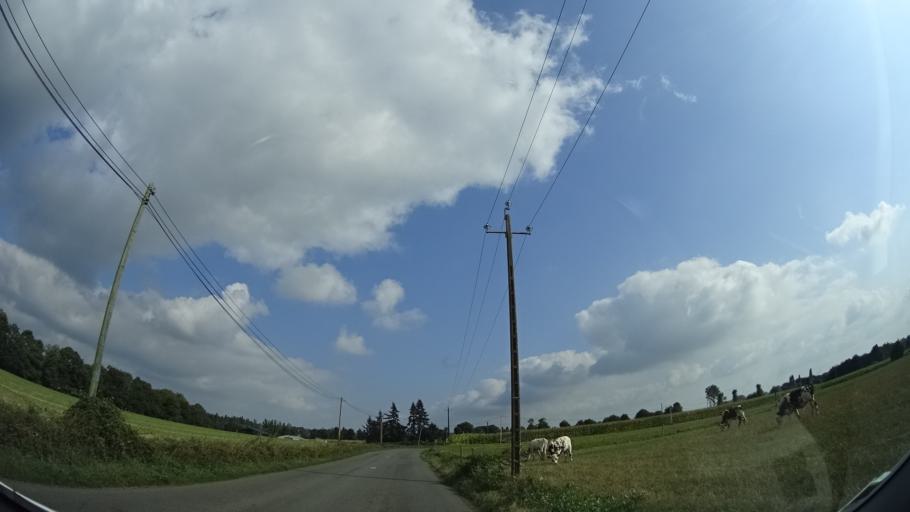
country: FR
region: Brittany
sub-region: Departement d'Ille-et-Vilaine
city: Romille
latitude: 48.2078
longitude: -1.8963
